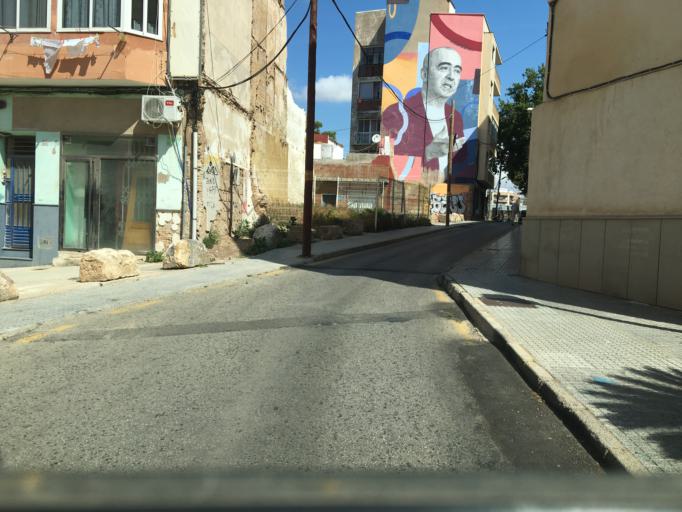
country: ES
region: Murcia
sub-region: Murcia
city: Cartagena
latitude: 37.6036
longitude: -0.9802
